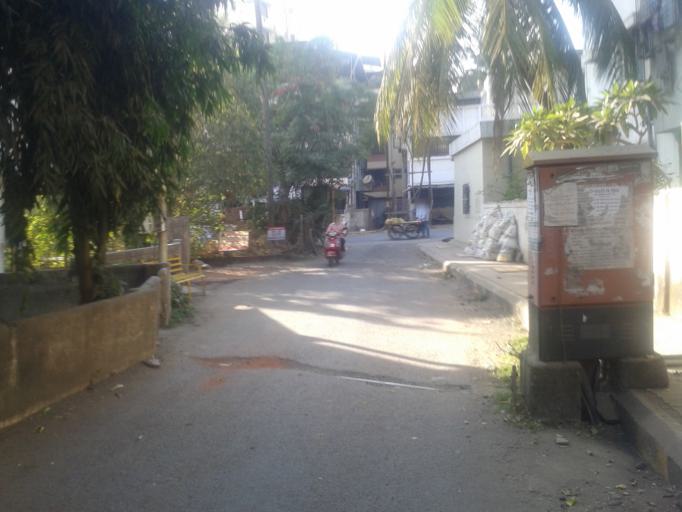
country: IN
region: Maharashtra
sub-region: Thane
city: Dombivli
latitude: 19.2051
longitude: 73.0892
